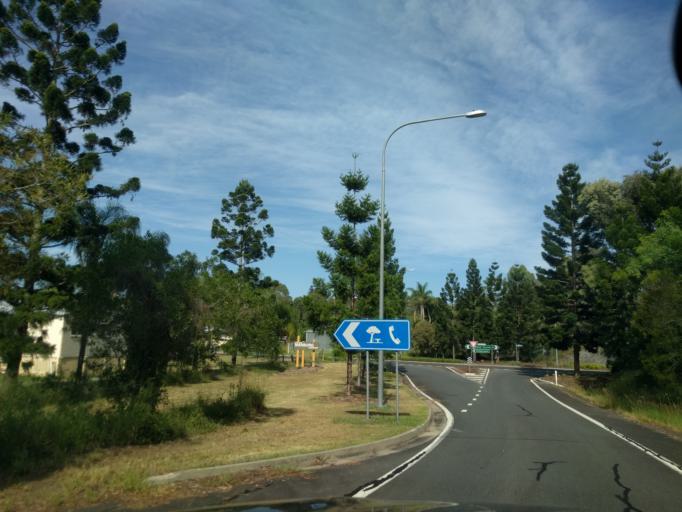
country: AU
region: Queensland
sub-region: Ipswich
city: Thagoona
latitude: -27.5636
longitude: 152.5974
